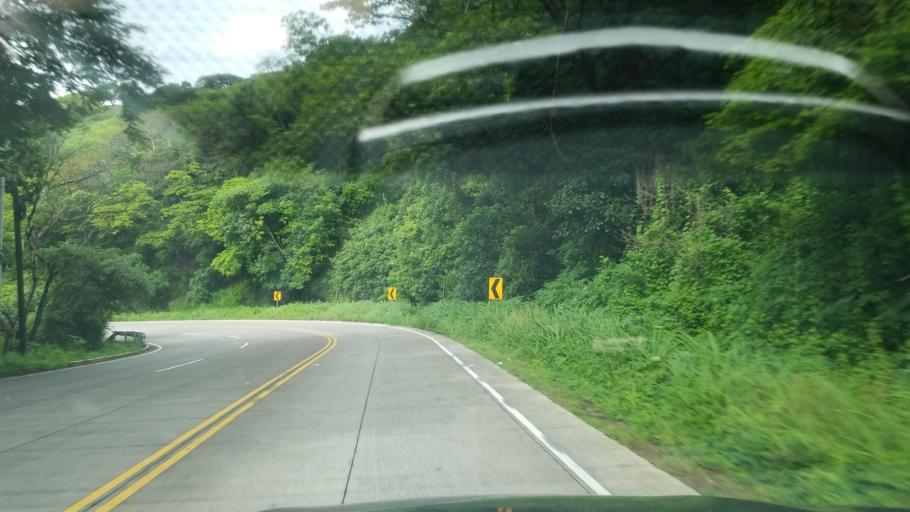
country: HN
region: Francisco Morazan
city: El Porvenir
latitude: 13.7091
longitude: -87.3185
